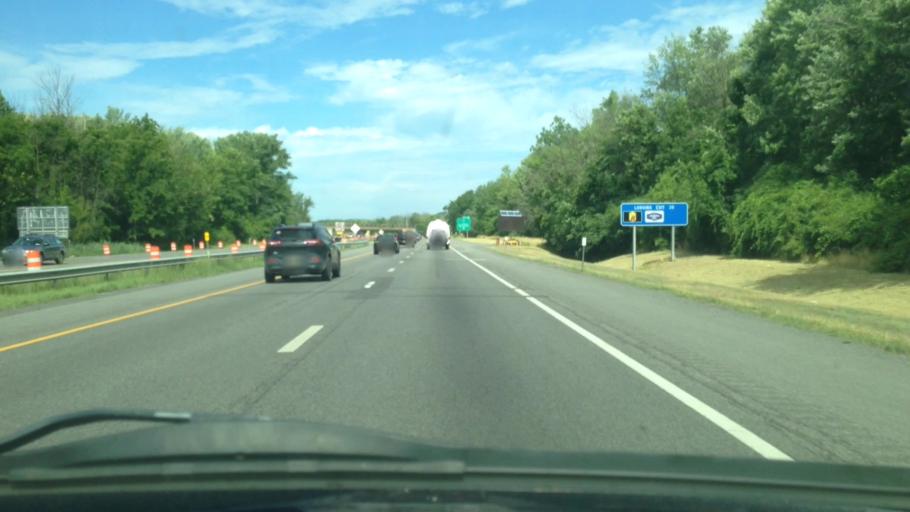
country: US
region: New York
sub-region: Onondaga County
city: Liverpool
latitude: 43.1136
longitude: -76.2077
